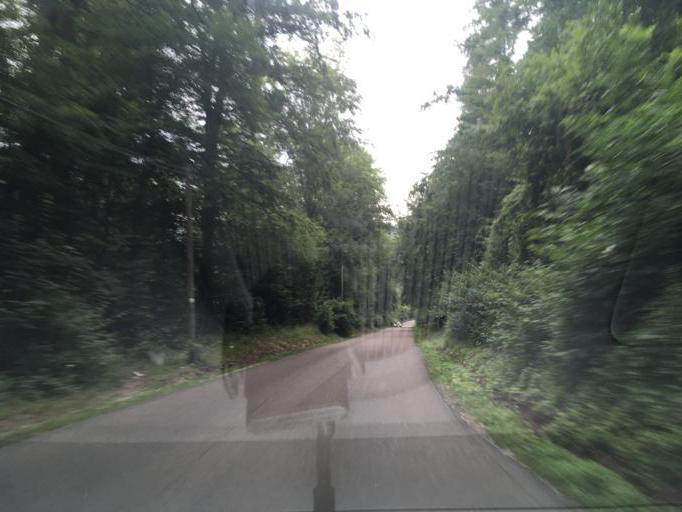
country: DE
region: Baden-Wuerttemberg
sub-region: Tuebingen Region
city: Kirchentellinsfurt
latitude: 48.5392
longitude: 9.1399
